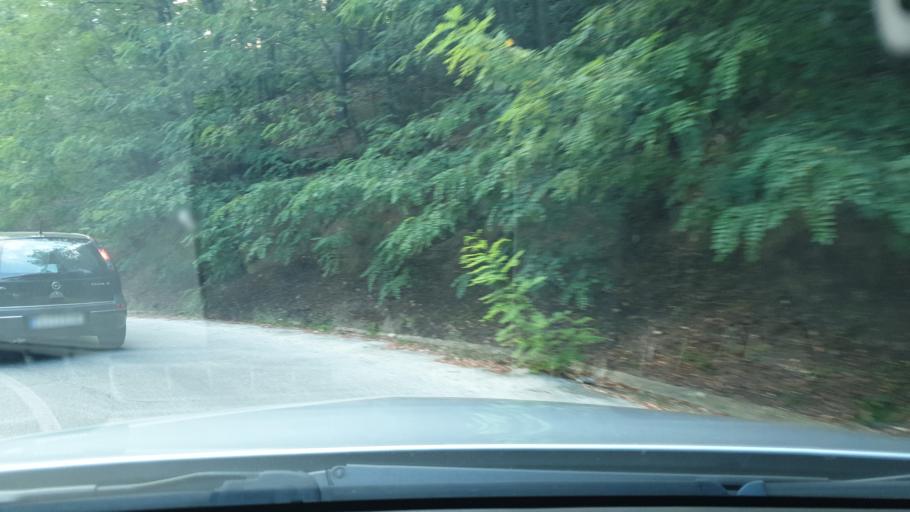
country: RS
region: Autonomna Pokrajina Vojvodina
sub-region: Juznobanatski Okrug
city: Vrsac
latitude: 45.1203
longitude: 21.3265
